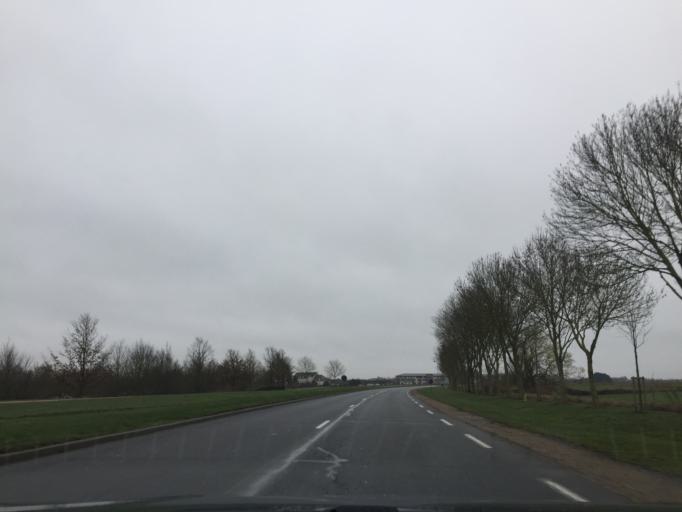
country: FR
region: Ile-de-France
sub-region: Departement de Seine-et-Marne
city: Magny-le-Hongre
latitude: 48.8718
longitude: 2.8051
